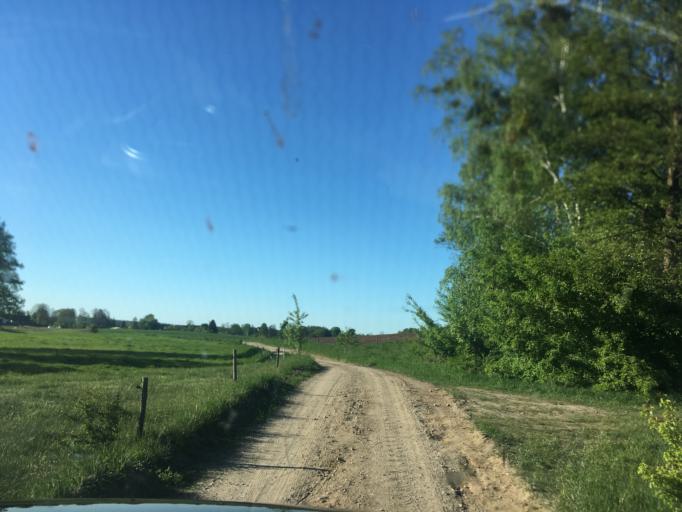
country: PL
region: Warmian-Masurian Voivodeship
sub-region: Powiat piski
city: Ruciane-Nida
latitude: 53.6588
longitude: 21.4823
